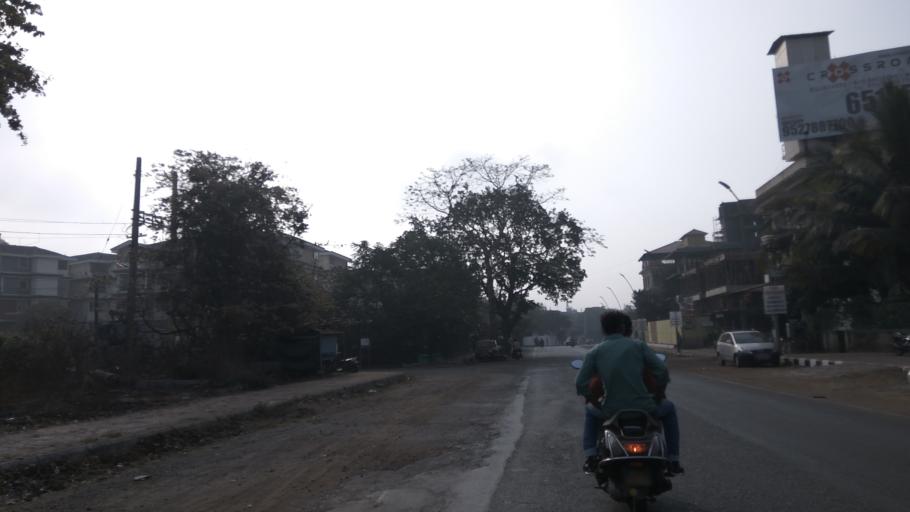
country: IN
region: Goa
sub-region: North Goa
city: Serula
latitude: 15.5374
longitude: 73.8191
